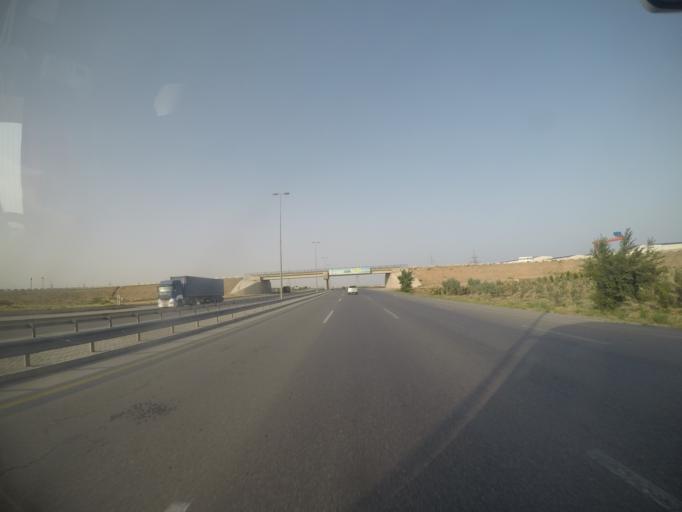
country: AZ
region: Baki
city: Puta
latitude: 40.2643
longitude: 49.6592
